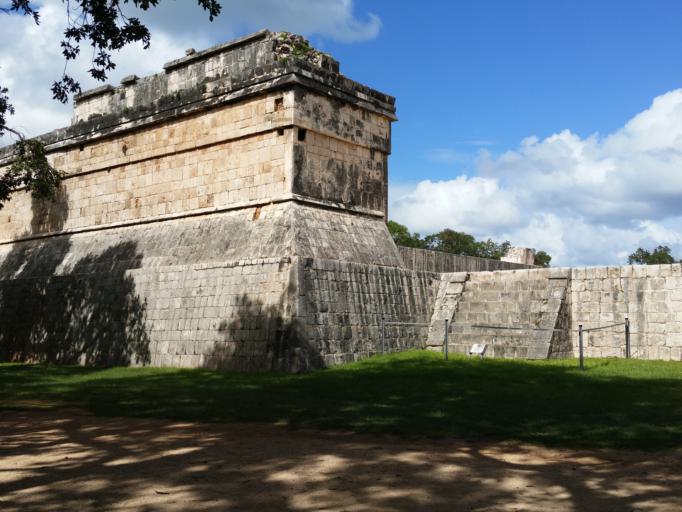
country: MX
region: Yucatan
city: Chichen-Itza
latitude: 20.6837
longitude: -88.5701
